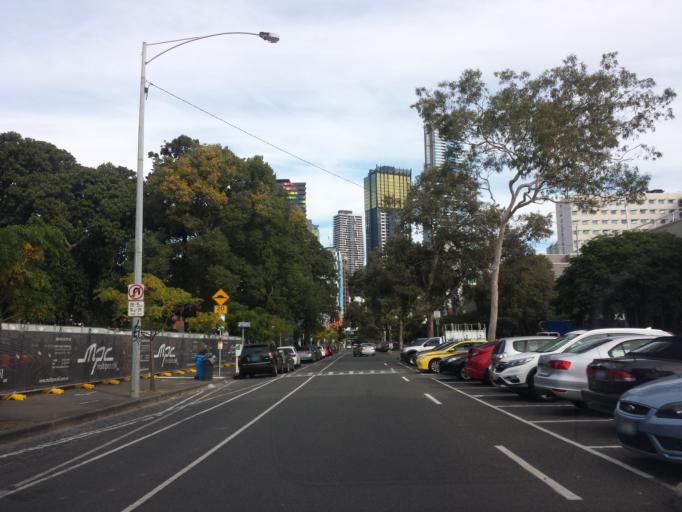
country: AU
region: Victoria
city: Carlton
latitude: -37.8018
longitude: 144.9623
